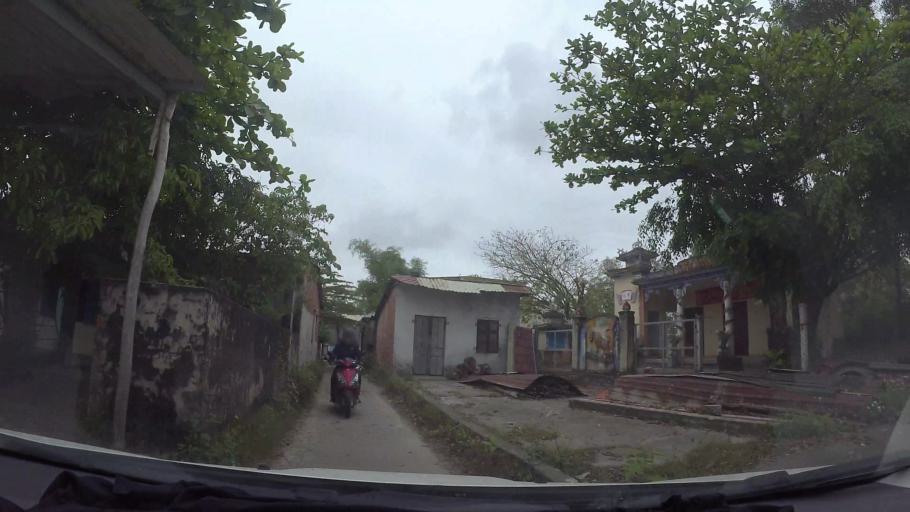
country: VN
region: Da Nang
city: Lien Chieu
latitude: 16.0884
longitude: 108.1055
